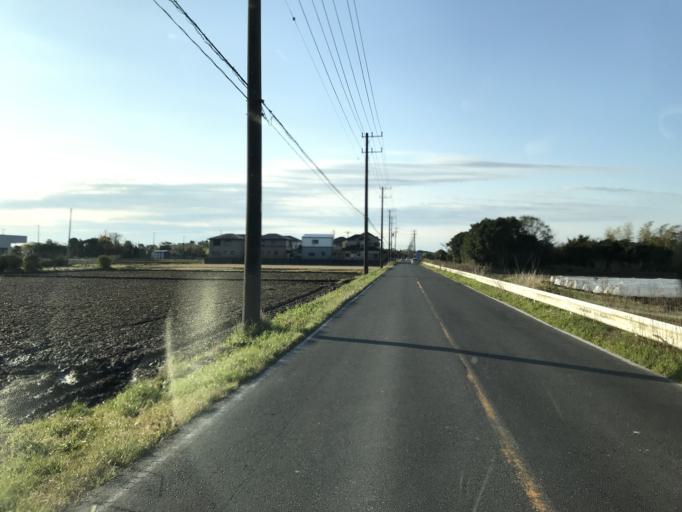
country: JP
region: Chiba
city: Yokaichiba
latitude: 35.6982
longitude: 140.5648
